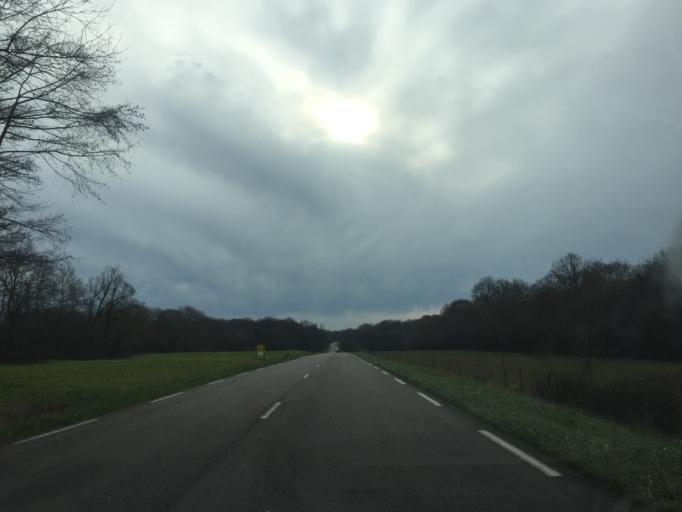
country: FR
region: Franche-Comte
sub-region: Departement du Jura
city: Mont-sous-Vaudrey
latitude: 46.9143
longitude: 5.5205
